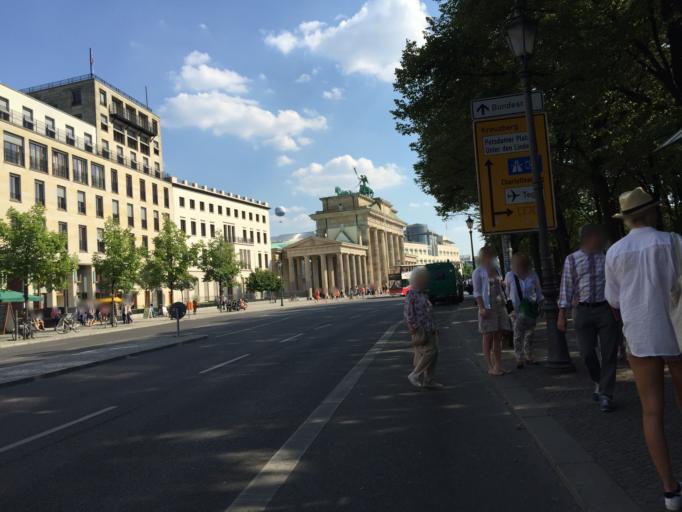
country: DE
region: Berlin
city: Tiergarten Bezirk
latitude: 52.5173
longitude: 13.3770
